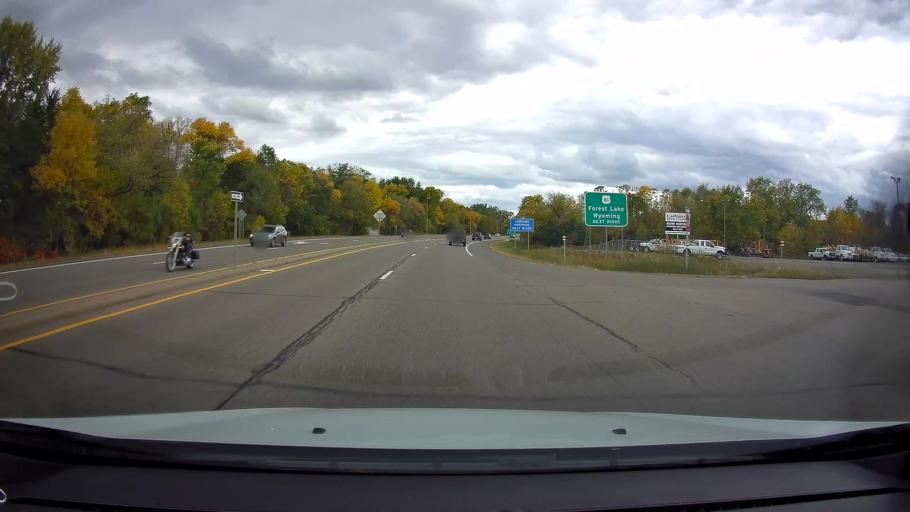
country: US
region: Minnesota
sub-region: Washington County
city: Forest Lake
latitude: 45.2927
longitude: -92.9769
